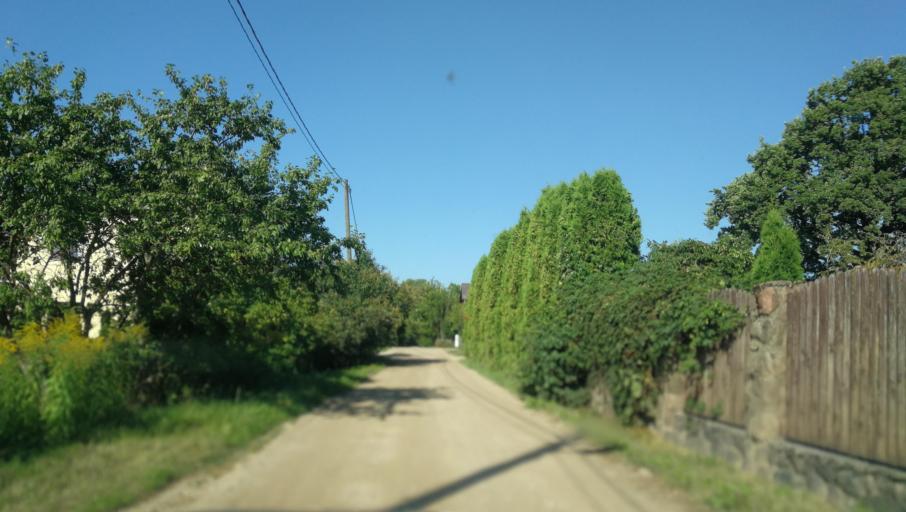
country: LV
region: Cesu Rajons
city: Cesis
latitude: 57.3162
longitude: 25.2981
